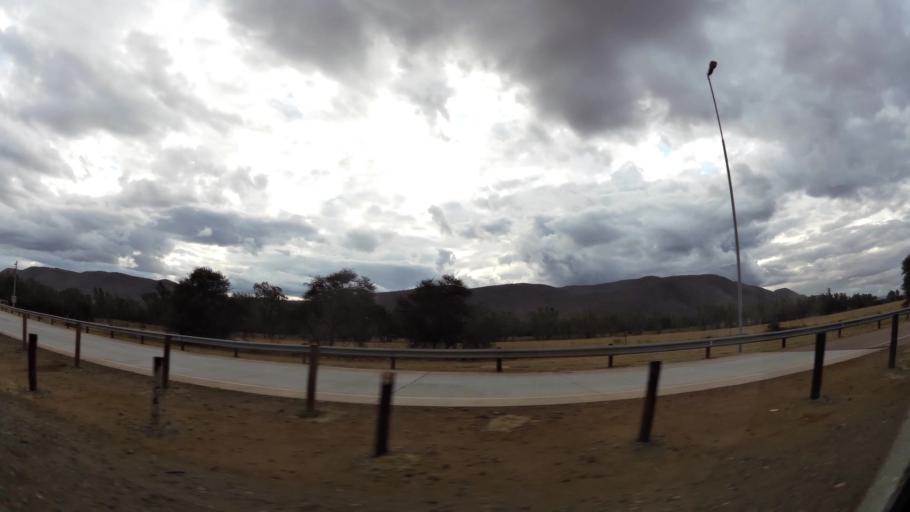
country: ZA
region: Limpopo
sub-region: Waterberg District Municipality
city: Mokopane
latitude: -24.2726
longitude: 28.9803
